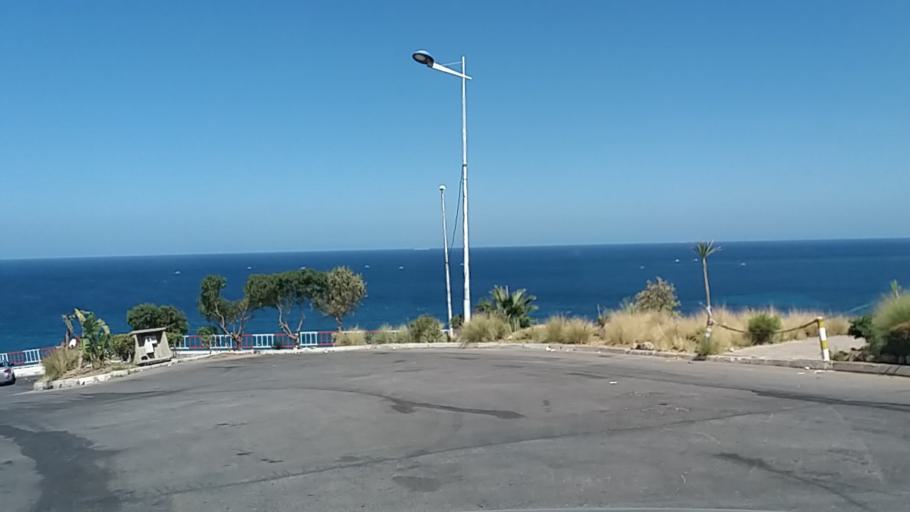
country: MA
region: Tanger-Tetouan
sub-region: Tanger-Assilah
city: Tangier
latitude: 35.7933
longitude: -5.7535
